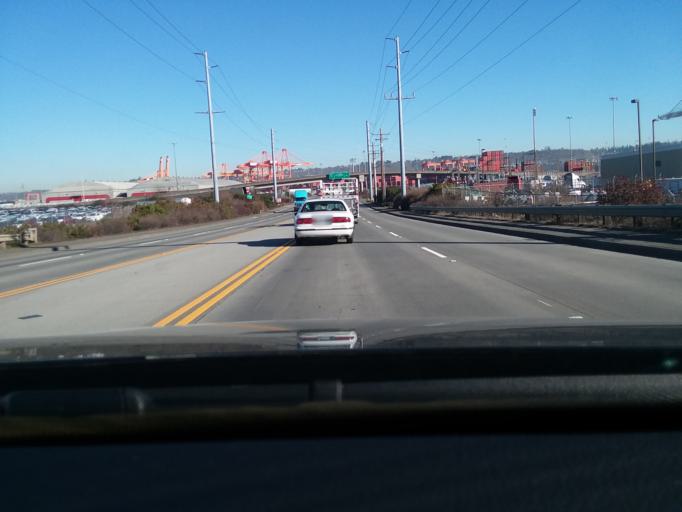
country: US
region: Washington
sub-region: Pierce County
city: Fife
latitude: 47.2503
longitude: -122.3855
